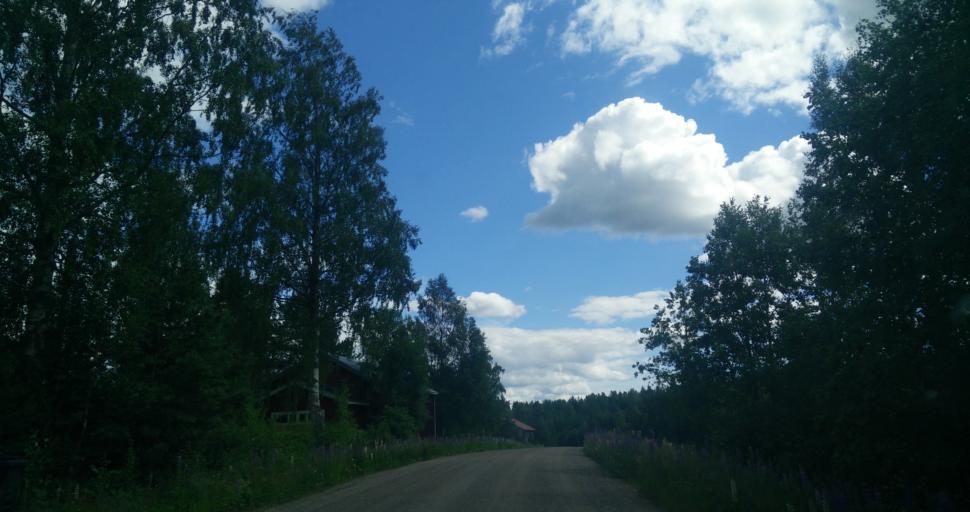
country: SE
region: Gaevleborg
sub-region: Nordanstigs Kommun
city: Bergsjoe
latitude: 62.0689
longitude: 16.7702
